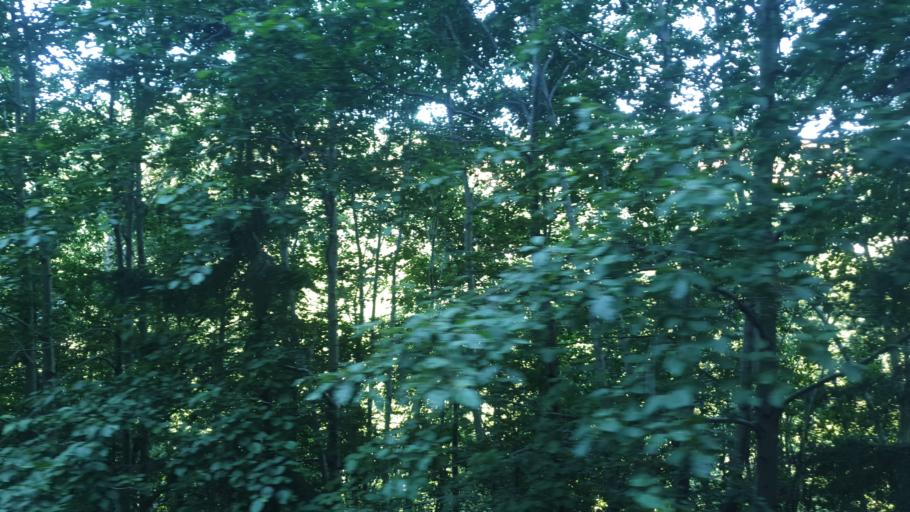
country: NO
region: Sor-Trondelag
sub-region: Meldal
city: Meldal
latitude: 63.1665
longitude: 9.7416
